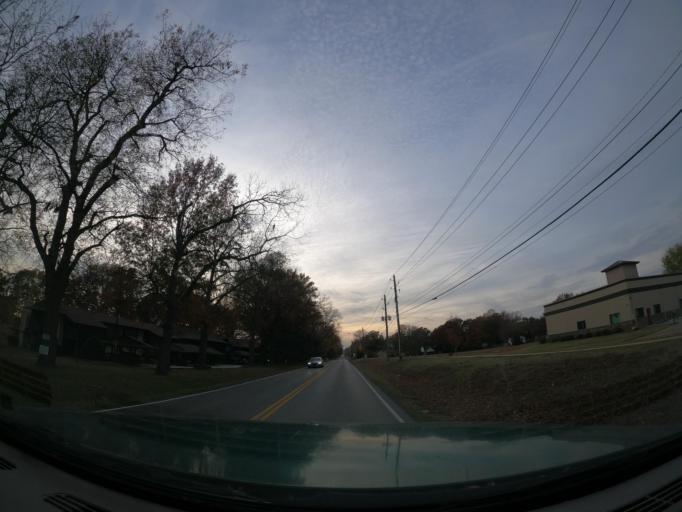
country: US
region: Oklahoma
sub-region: Tulsa County
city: Broken Arrow
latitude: 35.9738
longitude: -95.7990
